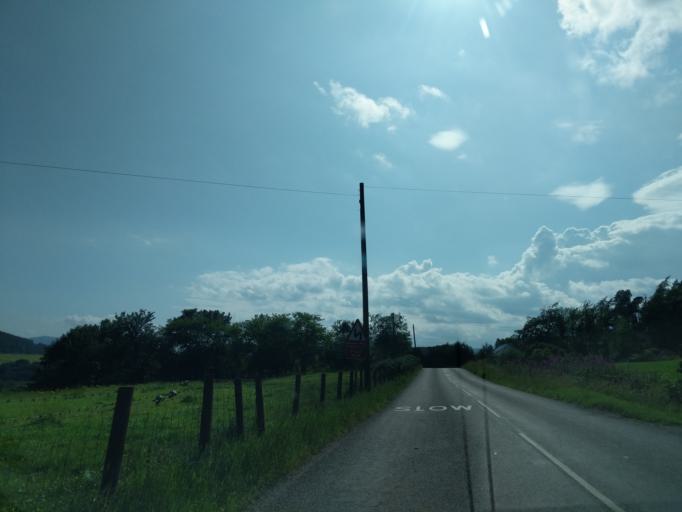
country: GB
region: Scotland
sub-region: Moray
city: Rothes
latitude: 57.5443
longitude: -3.1746
